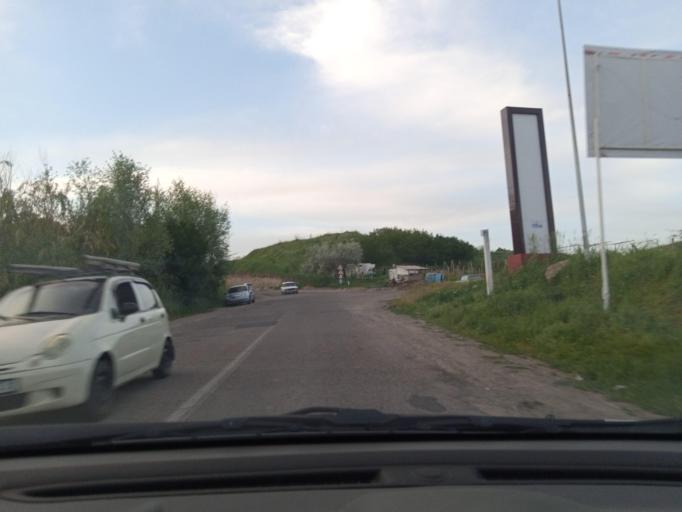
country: UZ
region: Toshkent
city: Parkent
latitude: 41.2466
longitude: 69.7335
